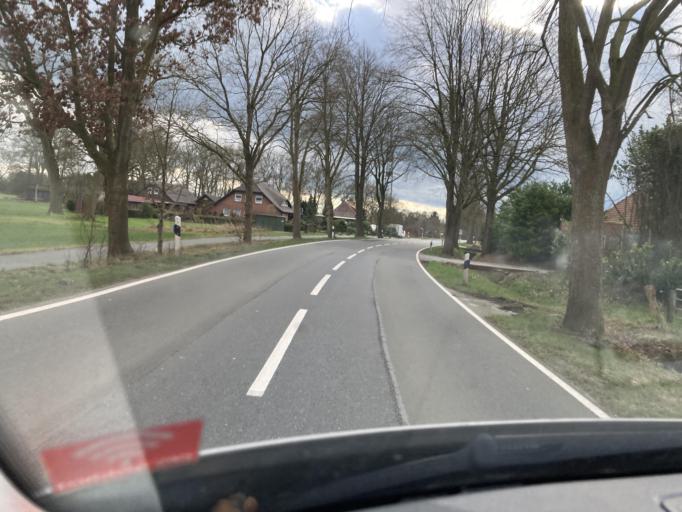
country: DE
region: Lower Saxony
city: Friedeburg
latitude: 53.3584
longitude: 7.8142
